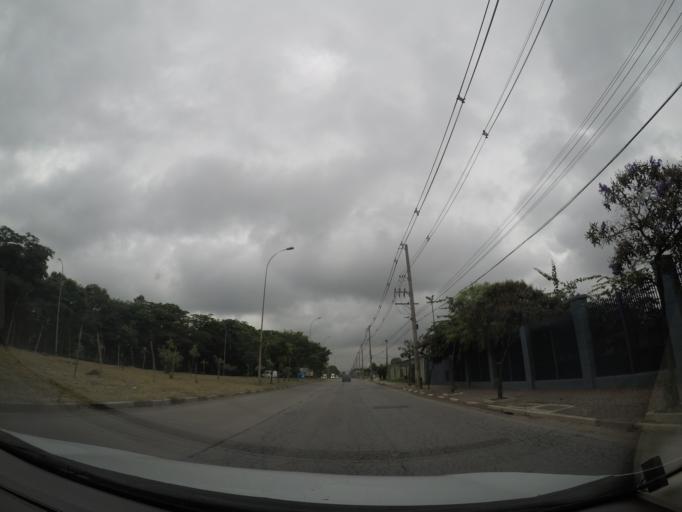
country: BR
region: Sao Paulo
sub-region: Guarulhos
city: Guarulhos
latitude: -23.4384
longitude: -46.4959
